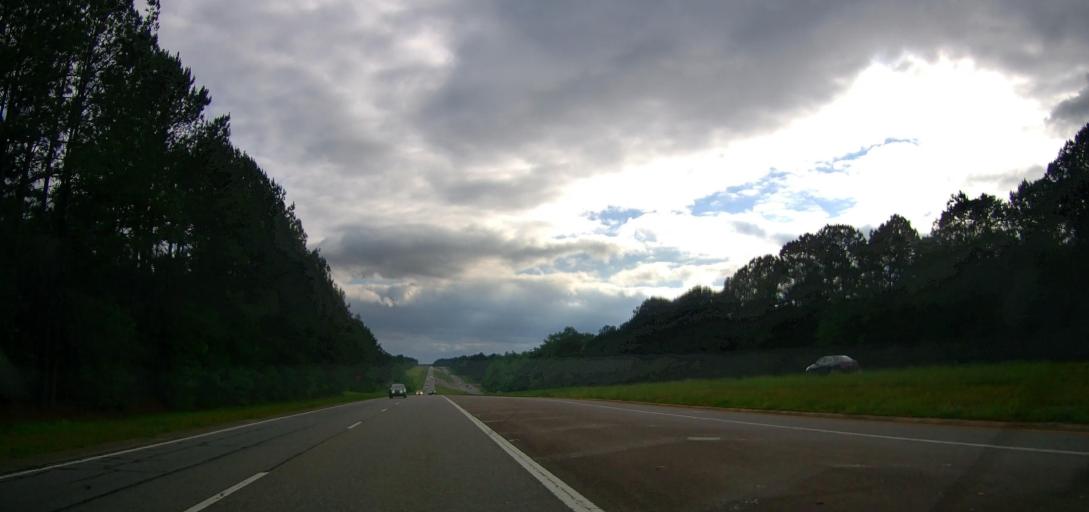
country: US
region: Georgia
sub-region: Oconee County
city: Bogart
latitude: 33.9101
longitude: -83.5600
